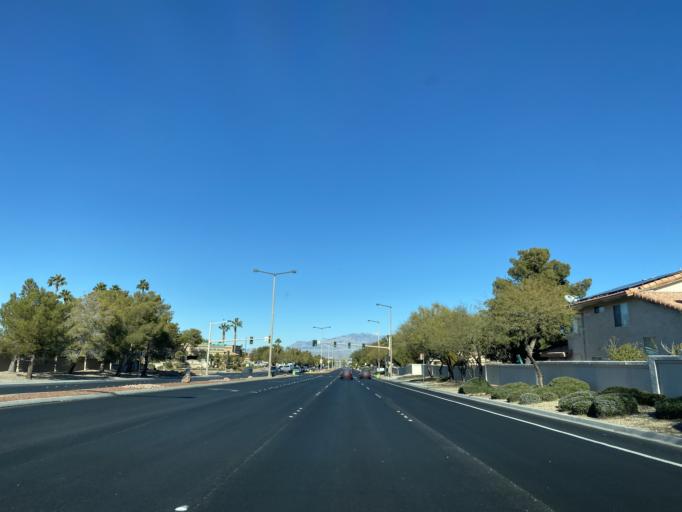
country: US
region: Nevada
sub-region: Clark County
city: Summerlin South
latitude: 36.2091
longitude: -115.2788
